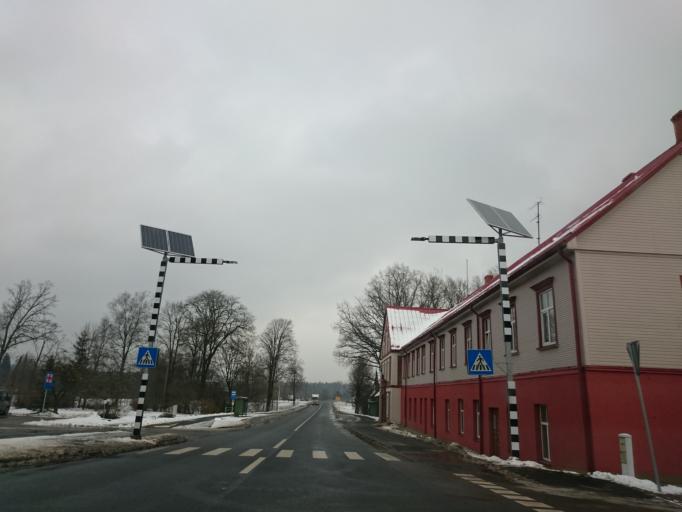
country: LV
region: Pargaujas
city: Stalbe
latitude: 57.3633
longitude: 24.9795
